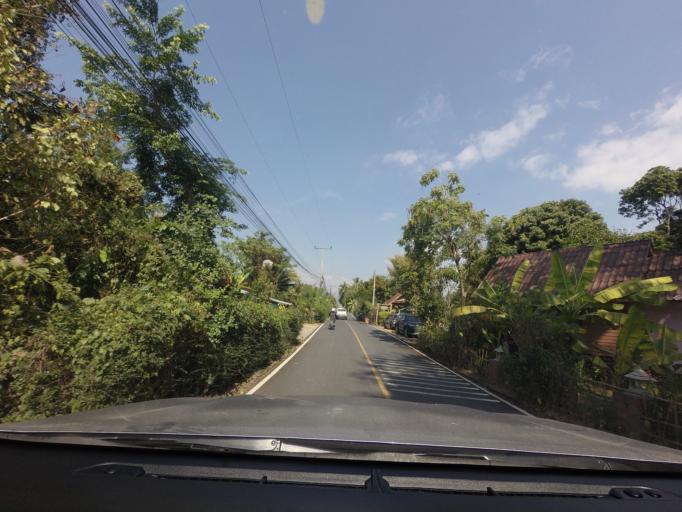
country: TH
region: Mae Hong Son
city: Wiang Nuea
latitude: 19.3751
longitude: 98.4454
